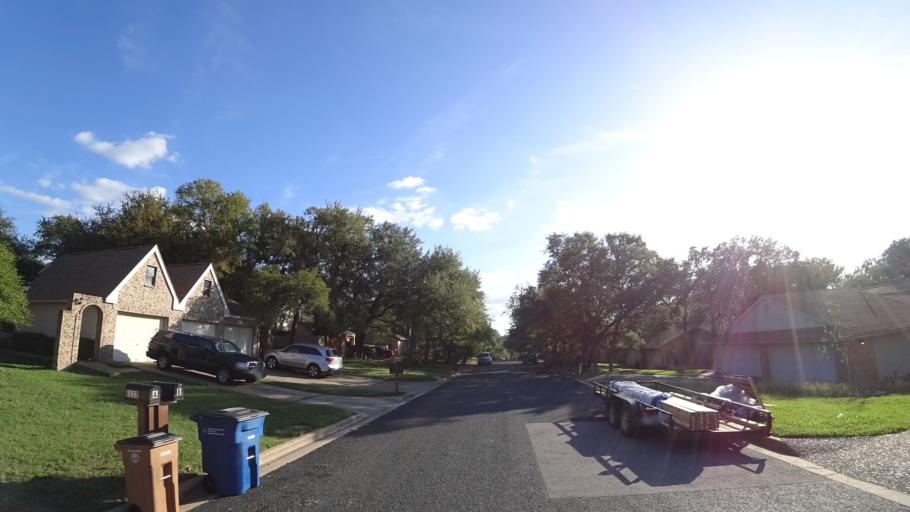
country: US
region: Texas
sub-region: Williamson County
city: Jollyville
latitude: 30.3679
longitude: -97.7479
